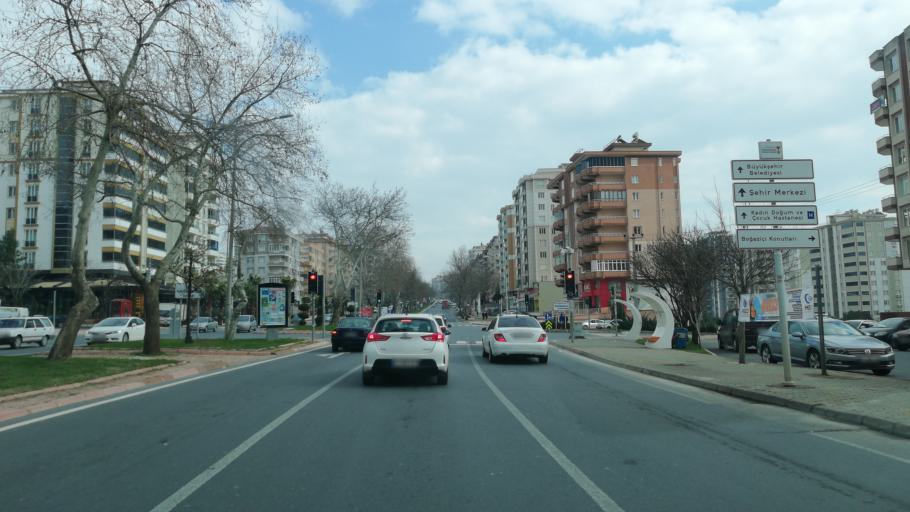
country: TR
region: Kahramanmaras
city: Kahramanmaras
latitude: 37.5917
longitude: 36.8674
